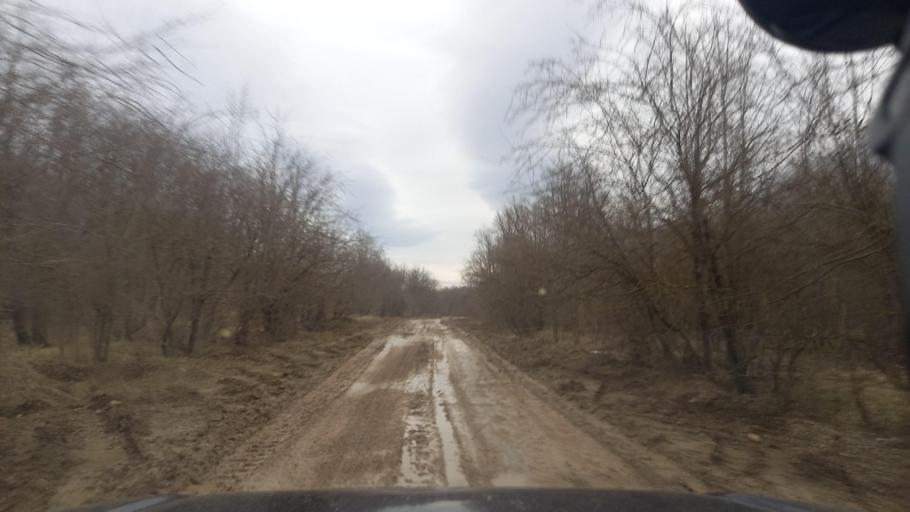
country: RU
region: Krasnodarskiy
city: Novodmitriyevskaya
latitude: 44.7525
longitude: 39.0008
